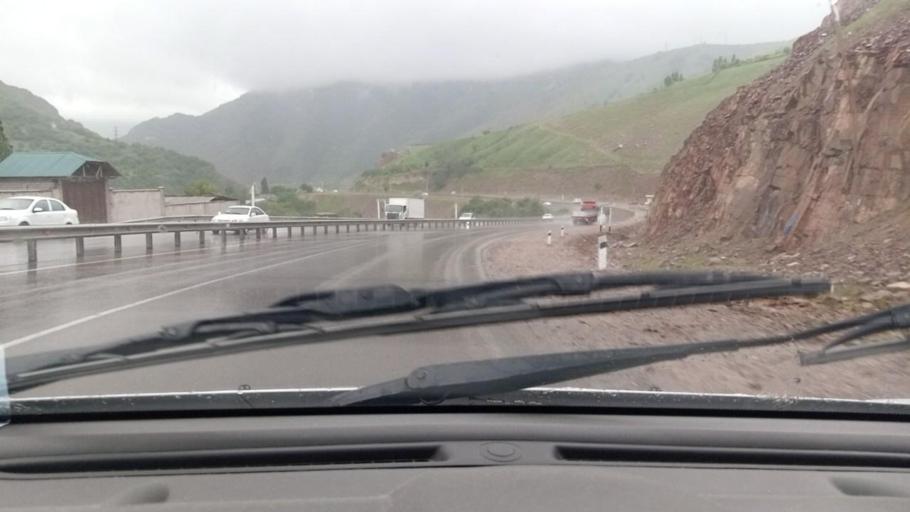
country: UZ
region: Toshkent
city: Angren
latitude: 41.1046
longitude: 70.3340
